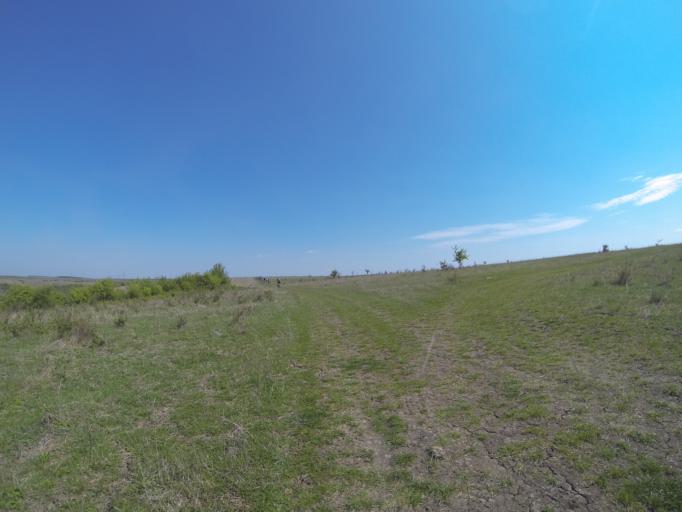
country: RO
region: Dolj
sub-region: Comuna Bradesti
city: Bradesti
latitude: 44.5351
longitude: 23.6360
